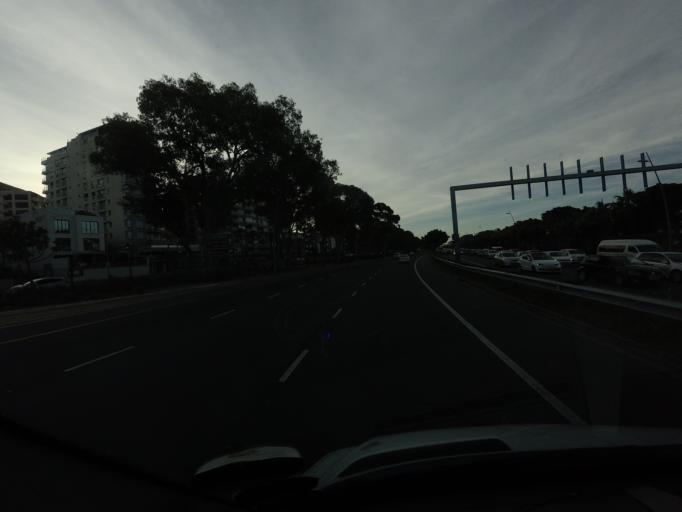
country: ZA
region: Western Cape
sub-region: City of Cape Town
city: Cape Town
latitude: -33.9113
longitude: 18.4162
